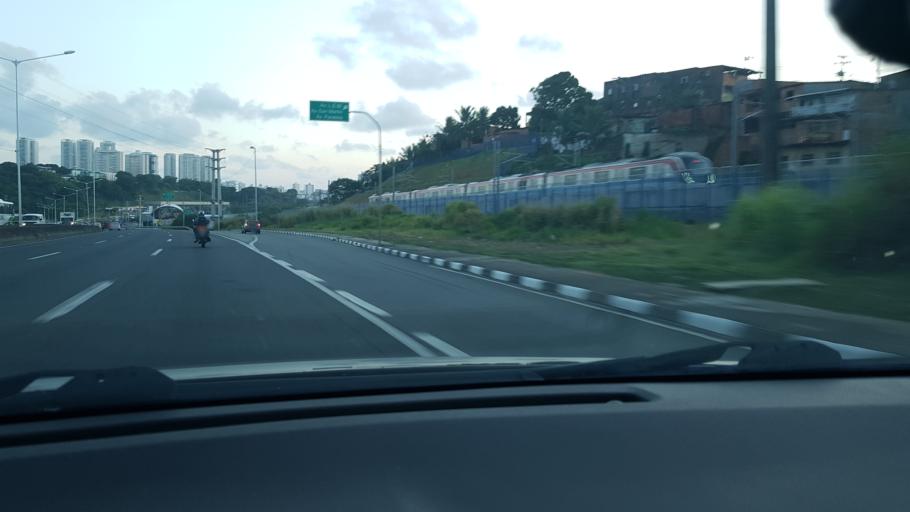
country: BR
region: Bahia
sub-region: Salvador
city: Salvador
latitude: -12.9510
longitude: -38.4710
